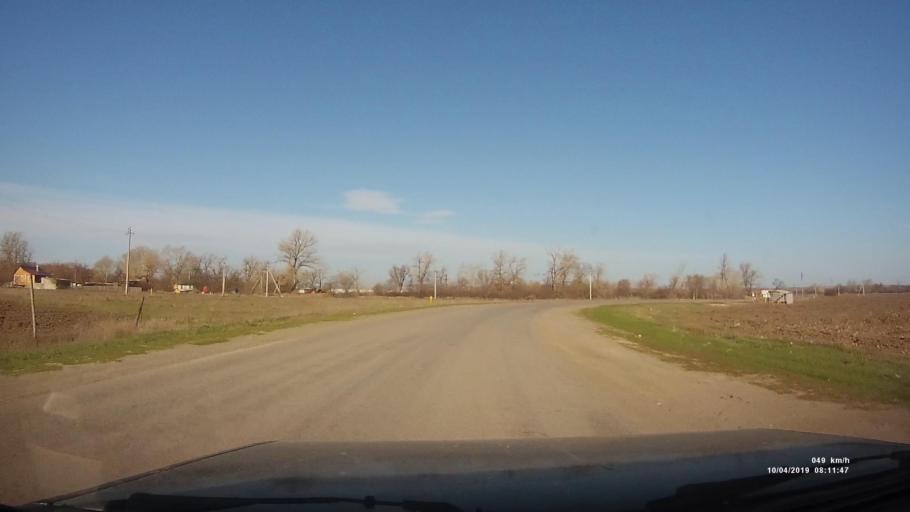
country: RU
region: Rostov
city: Staraya Stanitsa
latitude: 48.3595
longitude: 40.2630
